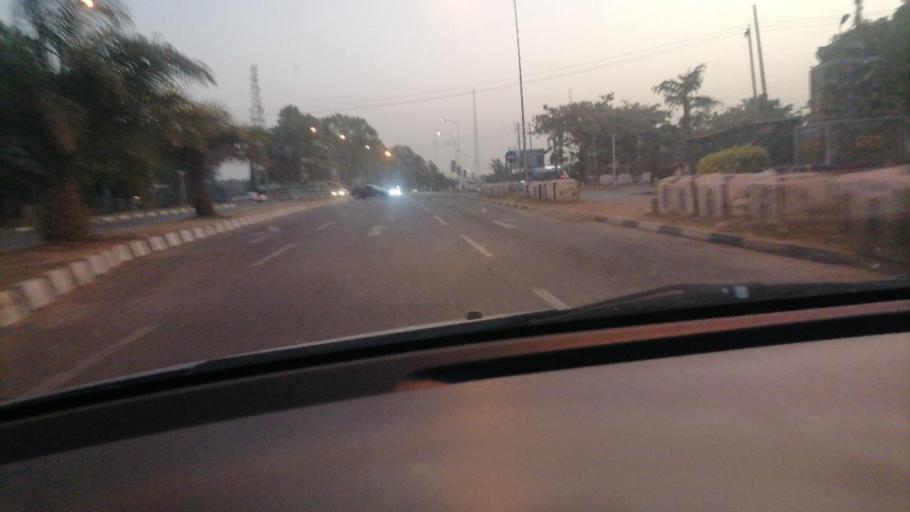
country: NG
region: Abuja Federal Capital Territory
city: Abuja
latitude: 9.0382
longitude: 7.4902
